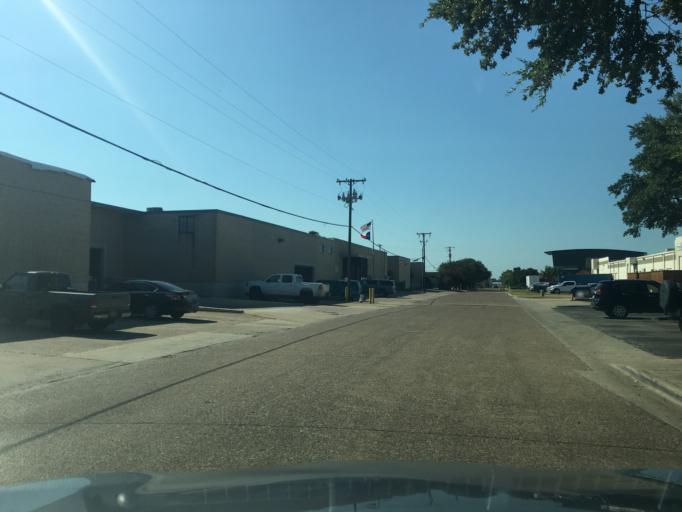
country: US
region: Texas
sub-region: Dallas County
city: Addison
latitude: 32.9639
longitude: -96.8376
